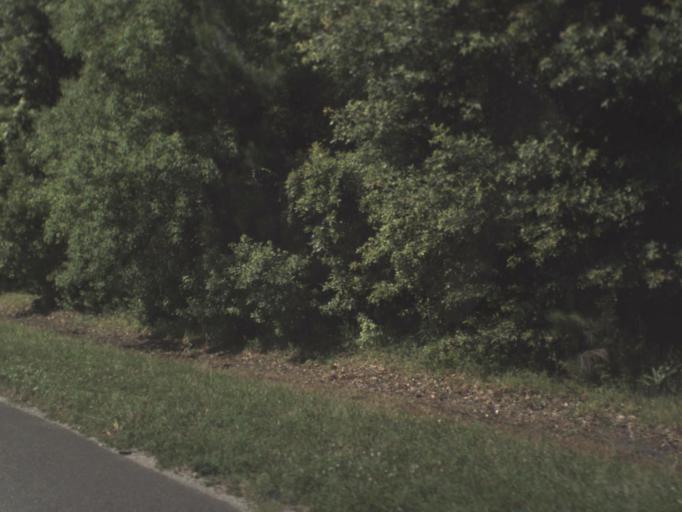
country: US
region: Florida
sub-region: Nassau County
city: Nassau Village-Ratliff
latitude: 30.4743
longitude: -81.7116
